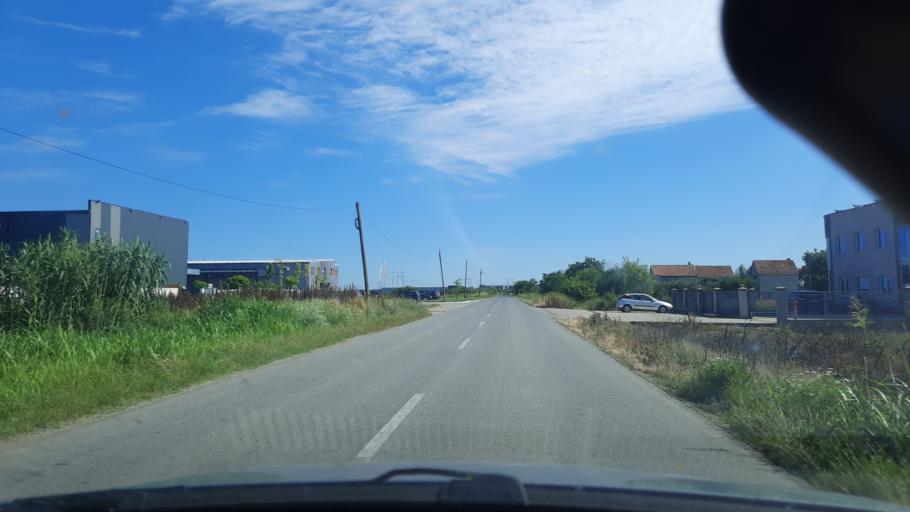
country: RS
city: Simanovci
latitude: 44.8588
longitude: 20.0983
